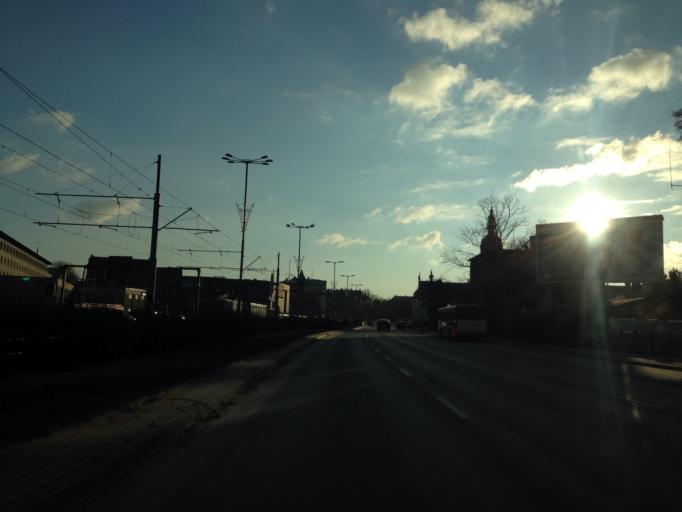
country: PL
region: Pomeranian Voivodeship
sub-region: Gdansk
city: Gdansk
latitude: 54.3574
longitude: 18.6459
